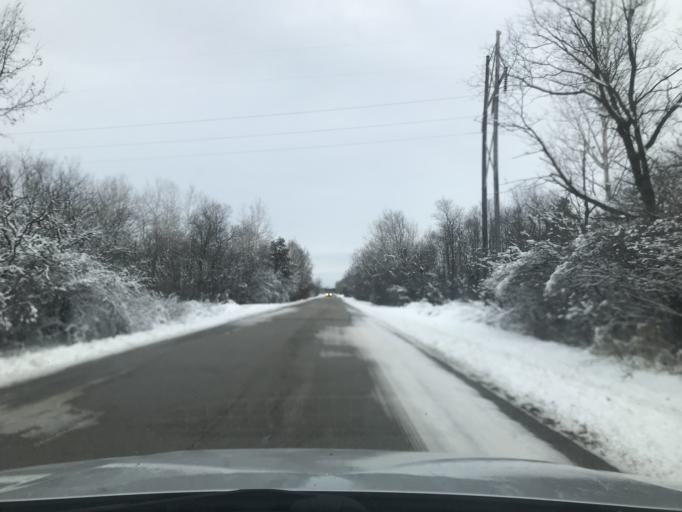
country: US
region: Wisconsin
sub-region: Marinette County
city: Peshtigo
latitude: 45.0864
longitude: -87.7222
